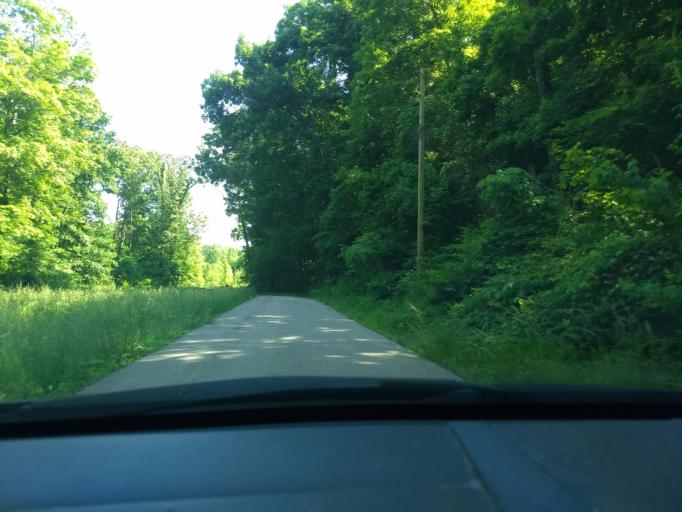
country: US
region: Indiana
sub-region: Floyd County
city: New Albany
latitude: 38.2727
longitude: -85.8671
